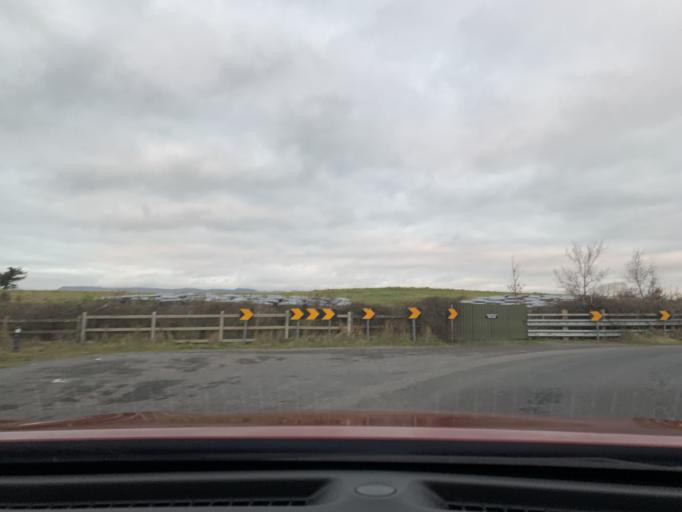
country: IE
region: Connaught
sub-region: Sligo
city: Sligo
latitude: 54.2786
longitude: -8.5134
